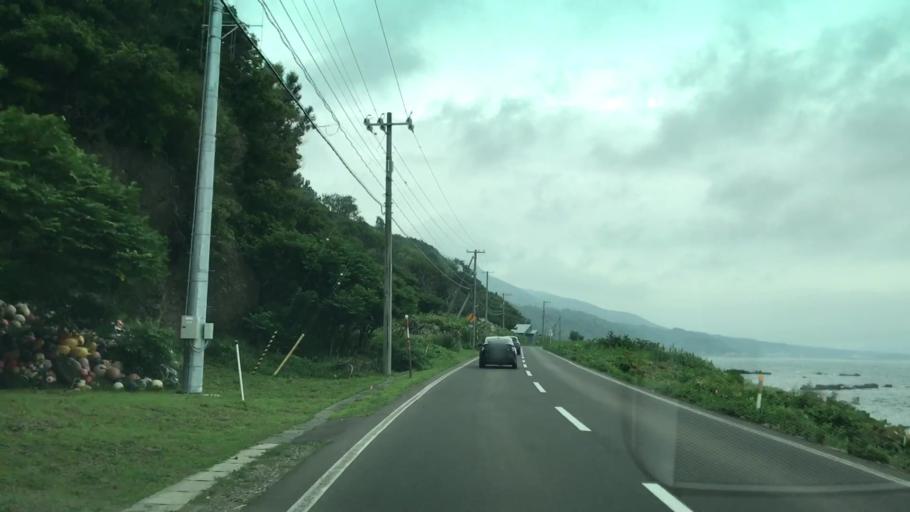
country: JP
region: Hokkaido
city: Iwanai
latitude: 42.8043
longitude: 140.3065
